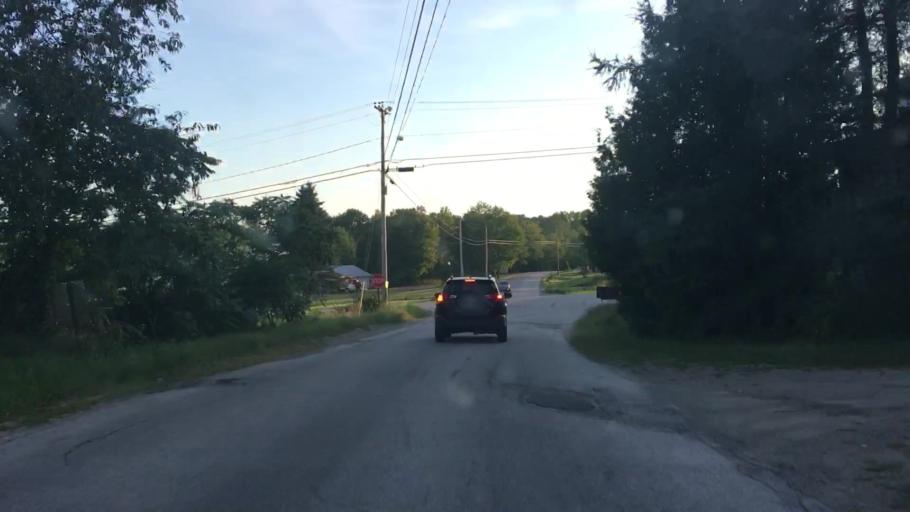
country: US
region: Maine
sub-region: Waldo County
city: Frankfort
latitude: 44.6757
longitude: -68.9184
